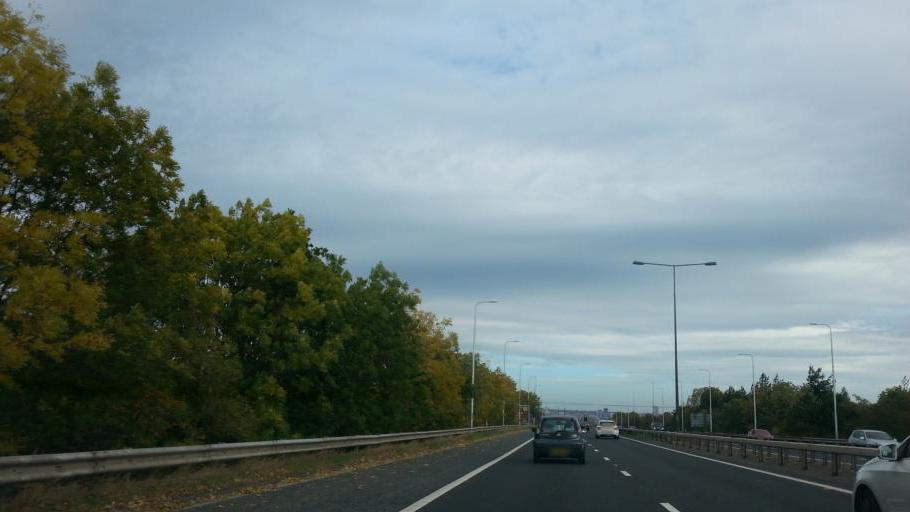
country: GB
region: England
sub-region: City and Borough of Leeds
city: Morley
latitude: 53.7671
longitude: -1.5935
